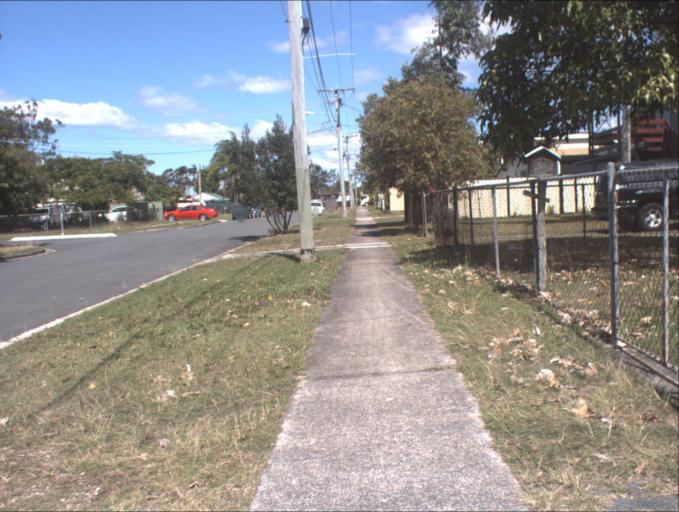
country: AU
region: Queensland
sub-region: Logan
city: Logan City
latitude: -27.6720
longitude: 153.1046
